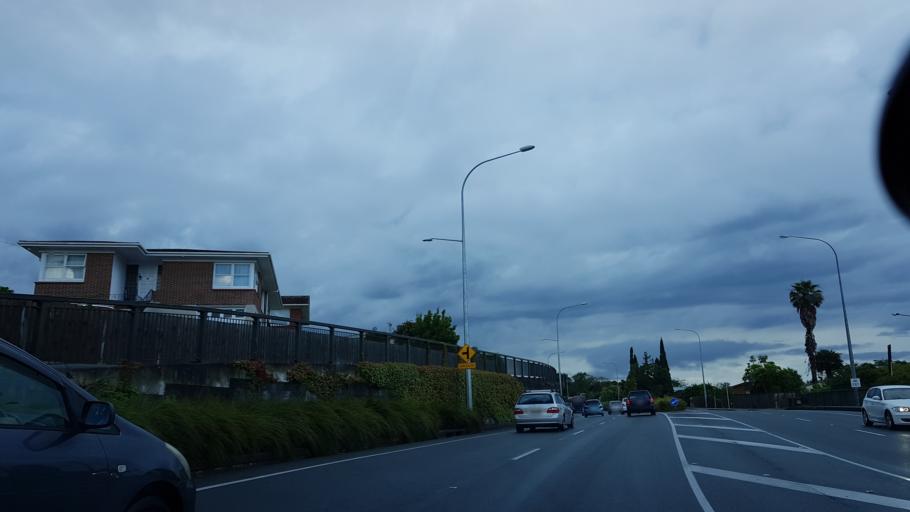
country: NZ
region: Auckland
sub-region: Auckland
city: North Shore
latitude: -36.7729
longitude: 174.7207
